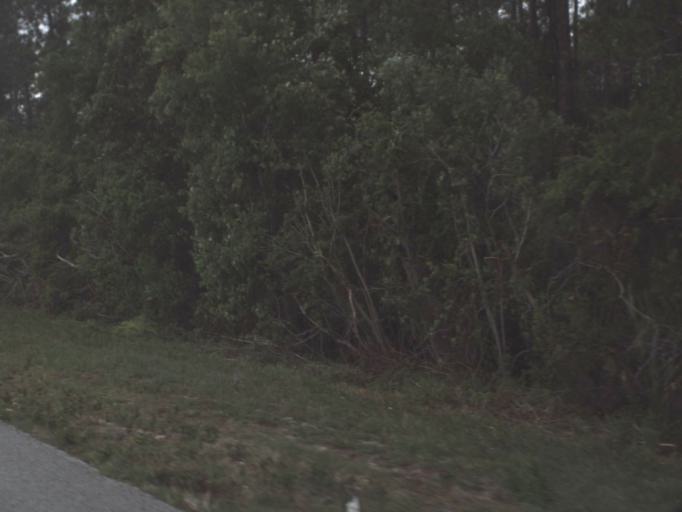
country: US
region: Florida
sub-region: Lake County
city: Lake Mack-Forest Hills
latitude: 28.9772
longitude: -81.4049
